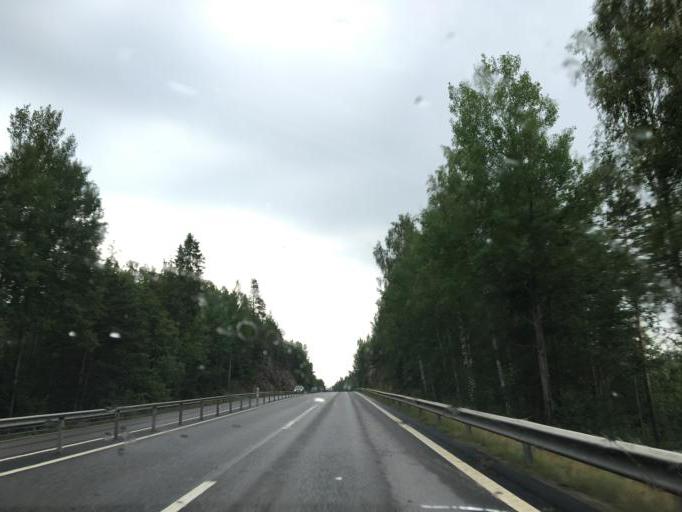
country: SE
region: OEstergoetland
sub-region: Norrkopings Kommun
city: Jursla
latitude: 58.7757
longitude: 16.1634
